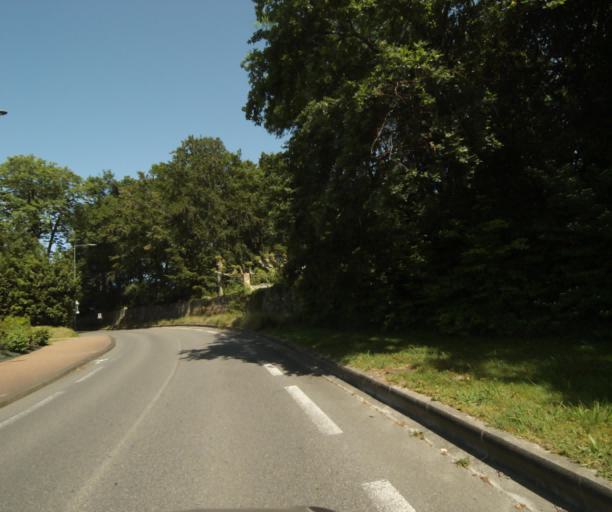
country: FR
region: Aquitaine
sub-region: Departement des Pyrenees-Atlantiques
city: Bayonne
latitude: 43.4756
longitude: -1.4554
